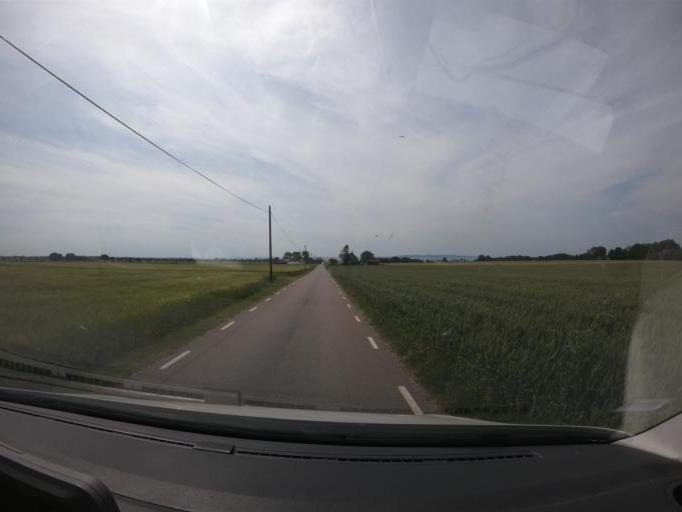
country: SE
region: Skane
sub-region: Angelholms Kommun
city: Vejbystrand
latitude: 56.3727
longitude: 12.7497
